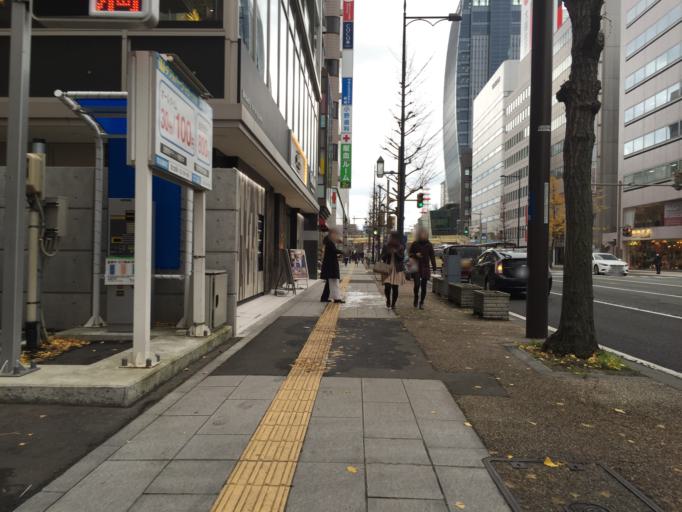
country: JP
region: Niigata
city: Niigata-shi
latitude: 37.9170
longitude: 139.0582
